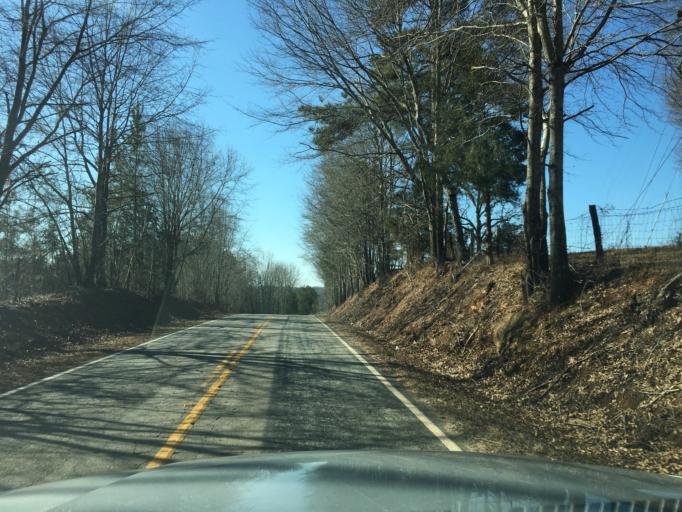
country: US
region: South Carolina
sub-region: Pickens County
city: Pickens
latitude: 34.8619
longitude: -82.7402
